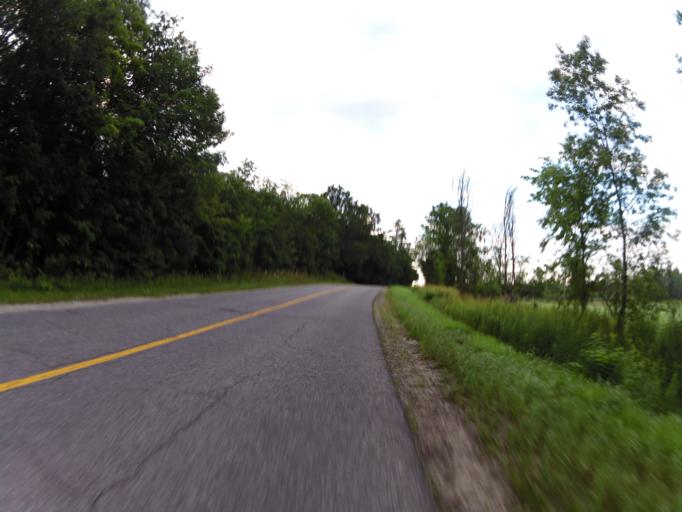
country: CA
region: Quebec
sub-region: Outaouais
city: Wakefield
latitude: 45.6888
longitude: -75.9437
